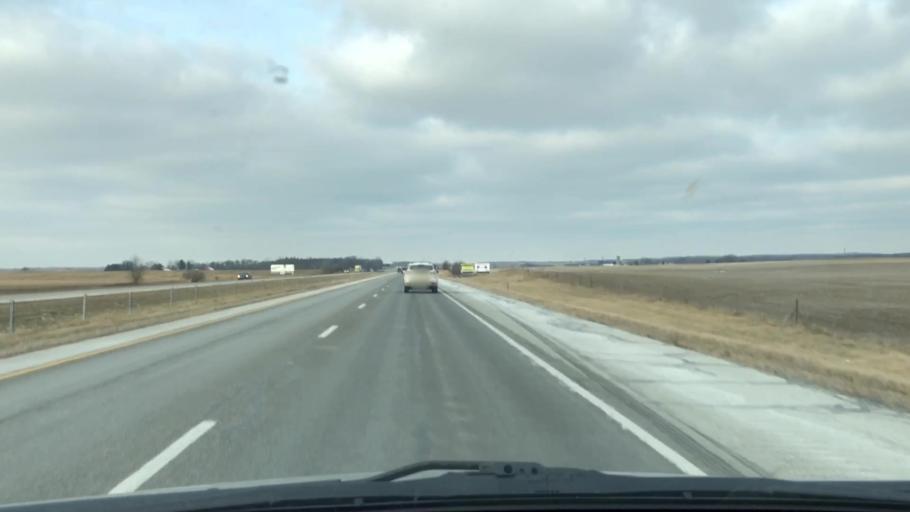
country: US
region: Indiana
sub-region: Steuben County
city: Angola
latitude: 41.5604
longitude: -85.0572
